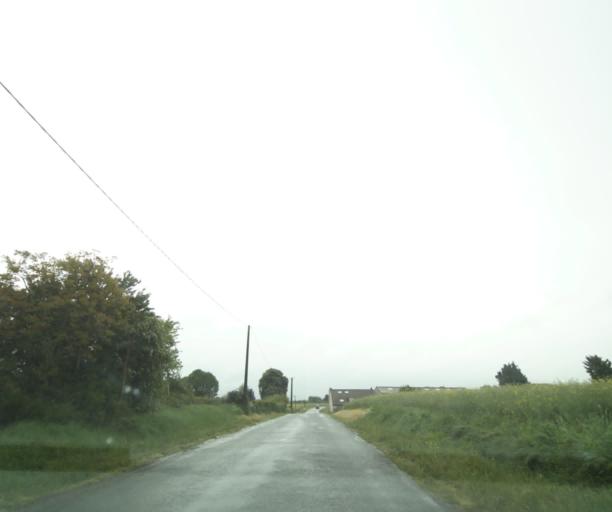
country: FR
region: Poitou-Charentes
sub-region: Departement de la Charente-Maritime
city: Corme-Royal
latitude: 45.7155
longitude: -0.8117
